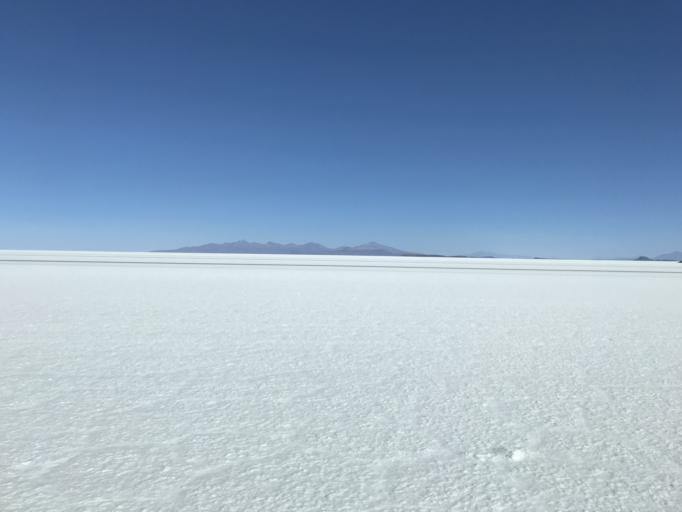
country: BO
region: Potosi
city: Colchani
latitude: -20.2387
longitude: -67.6171
